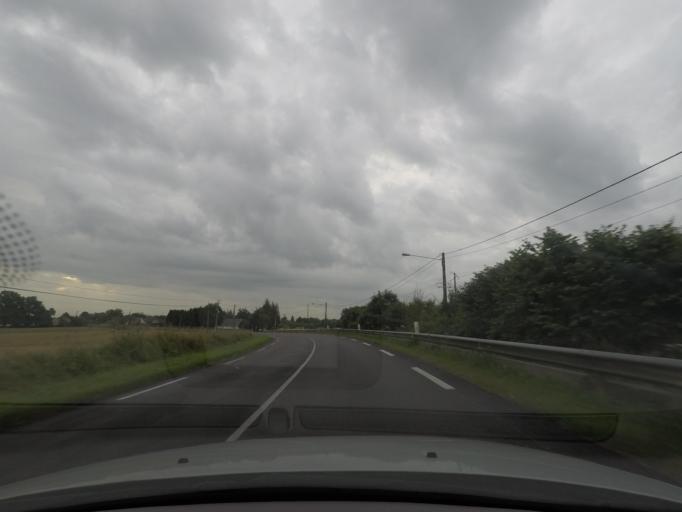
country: FR
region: Haute-Normandie
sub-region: Departement de la Seine-Maritime
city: Neufchatel-en-Bray
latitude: 49.7328
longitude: 1.5079
